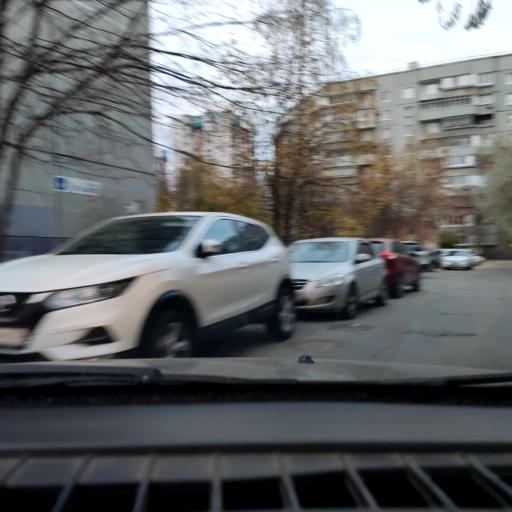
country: RU
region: Samara
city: Tol'yatti
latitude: 53.5451
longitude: 49.3417
